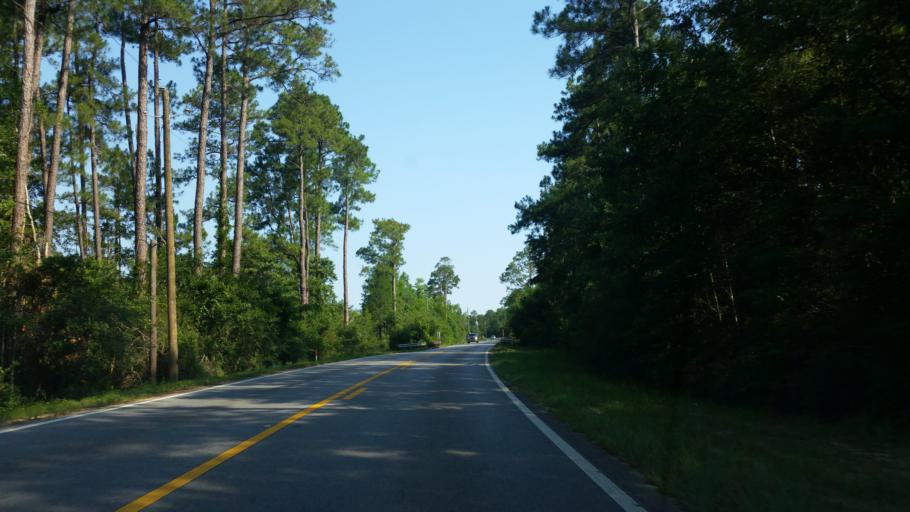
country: US
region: Florida
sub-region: Santa Rosa County
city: East Milton
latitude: 30.6033
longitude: -87.0080
